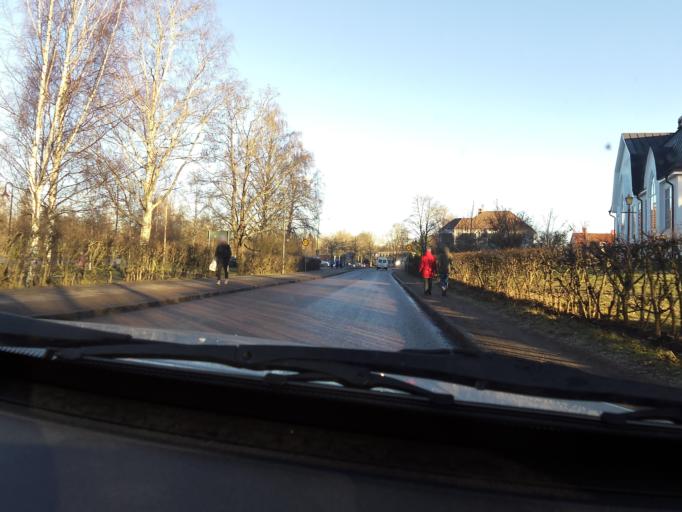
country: SE
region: Gaevleborg
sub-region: Gavle Kommun
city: Gavle
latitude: 60.6706
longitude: 17.1219
